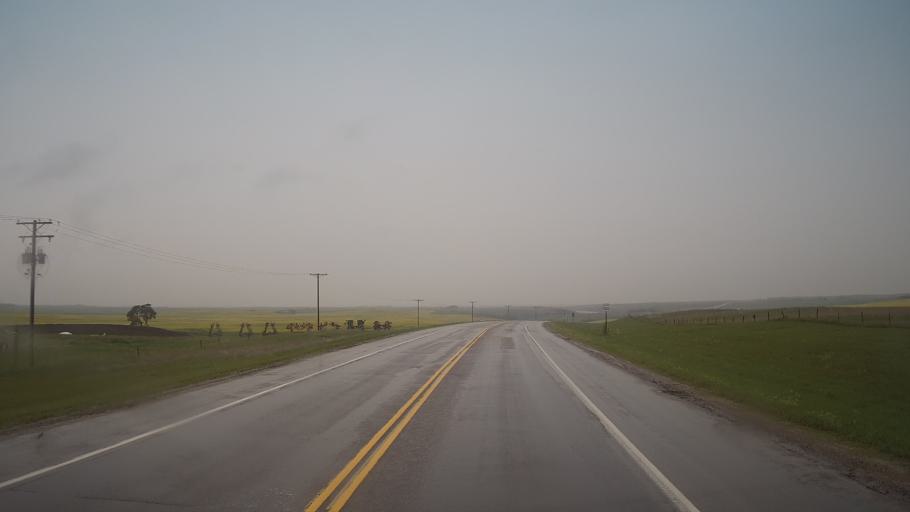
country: CA
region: Saskatchewan
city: Biggar
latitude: 52.0661
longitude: -107.9984
